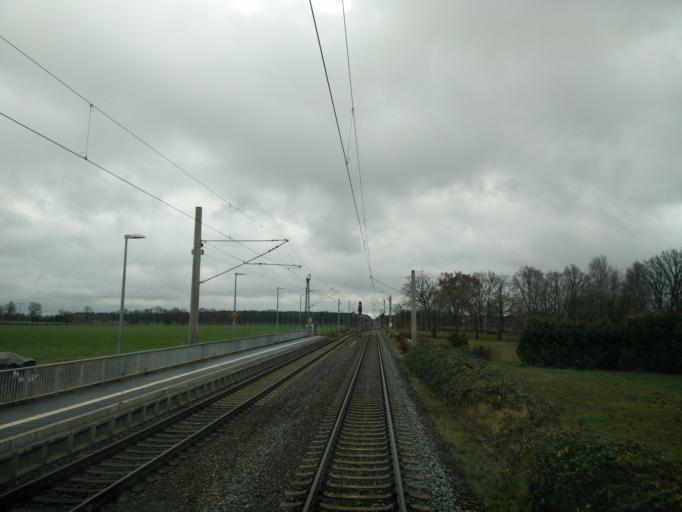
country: DE
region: Mecklenburg-Vorpommern
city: Rastow
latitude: 53.4559
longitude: 11.4325
